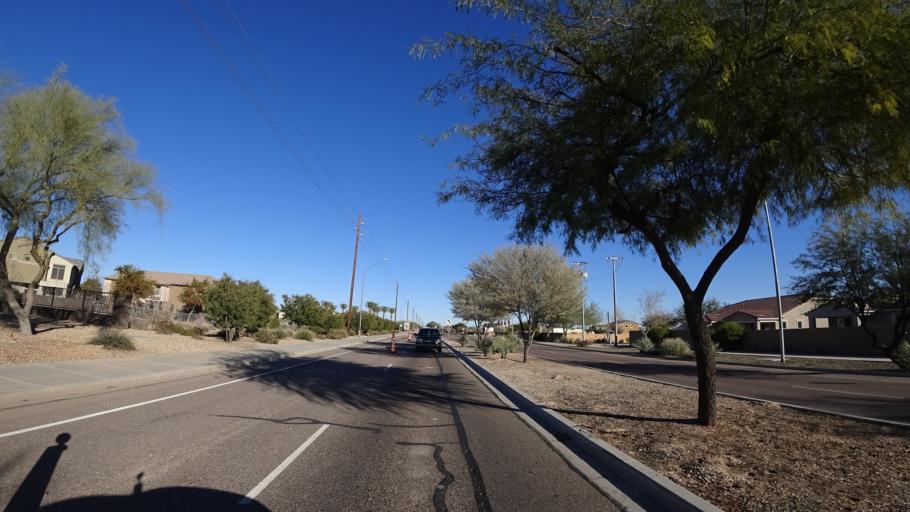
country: US
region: Arizona
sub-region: Maricopa County
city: Goodyear
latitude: 33.4502
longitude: -112.4231
